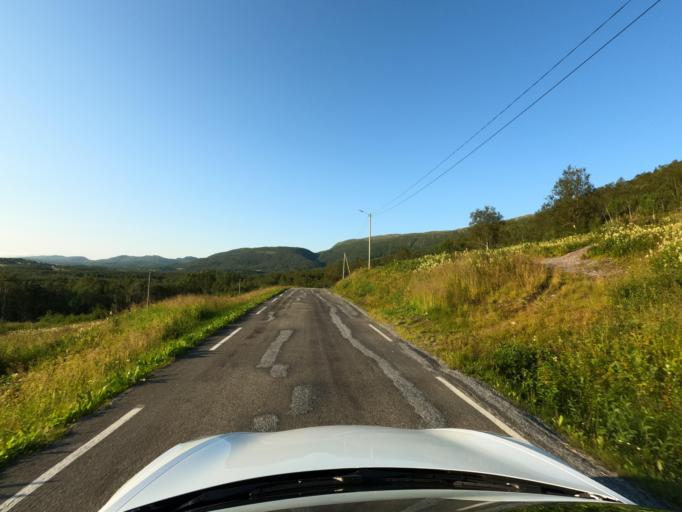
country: NO
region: Nordland
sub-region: Ballangen
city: Ballangen
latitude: 68.5208
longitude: 16.7599
